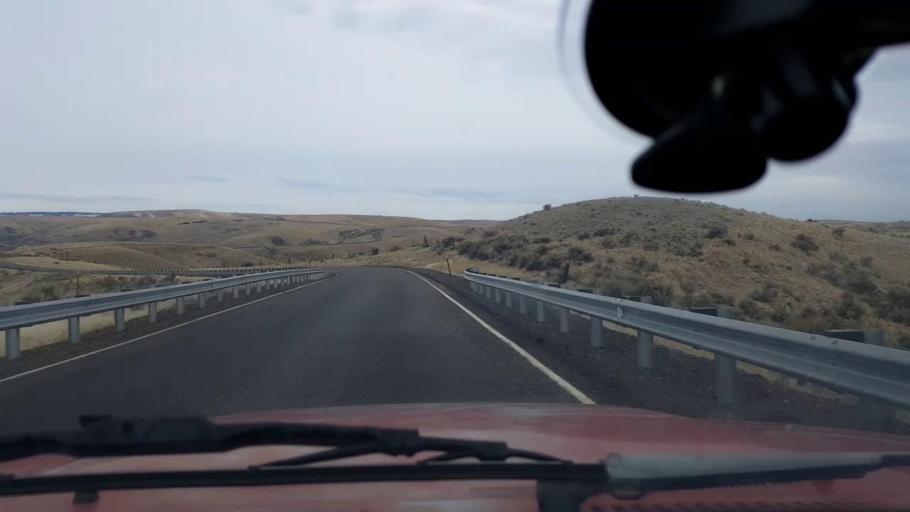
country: US
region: Washington
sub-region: Asotin County
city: Clarkston Heights-Vineland
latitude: 46.3347
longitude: -117.2860
